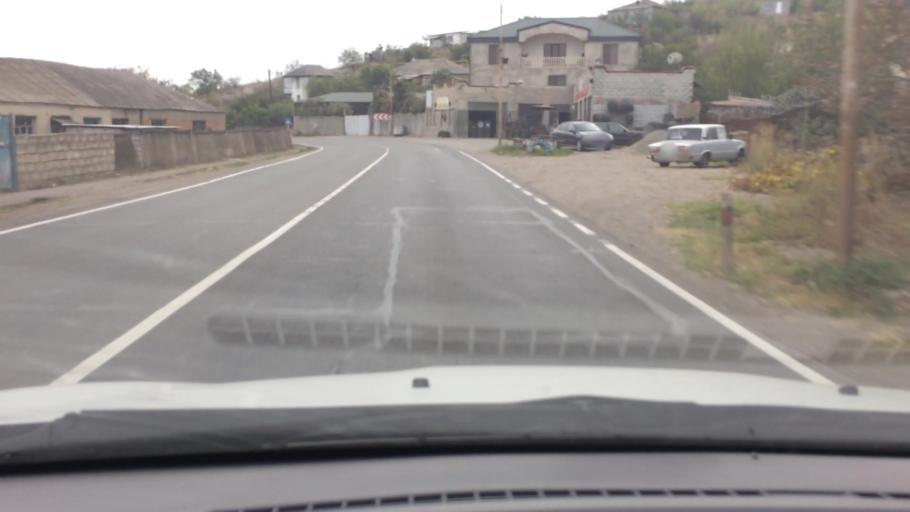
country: GE
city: Naghvarevi
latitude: 41.3687
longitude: 44.8378
